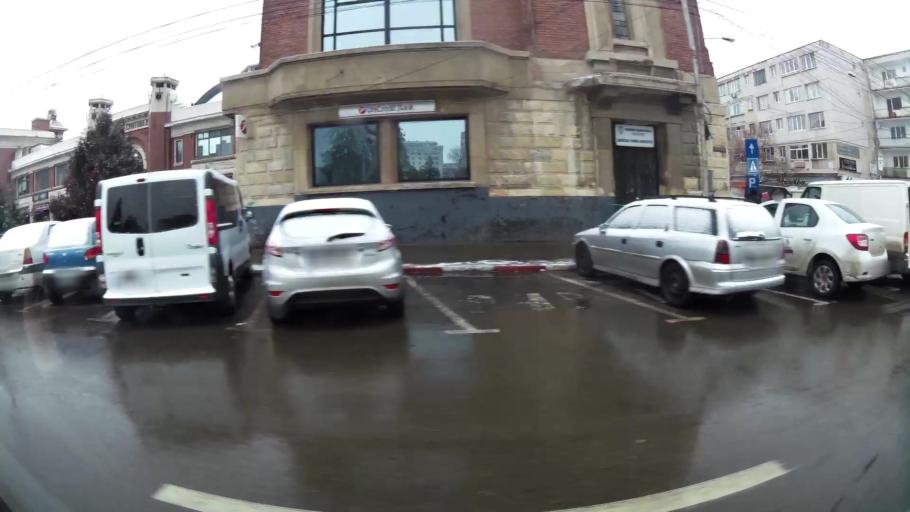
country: RO
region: Prahova
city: Ploiesti
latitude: 44.9430
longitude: 26.0213
